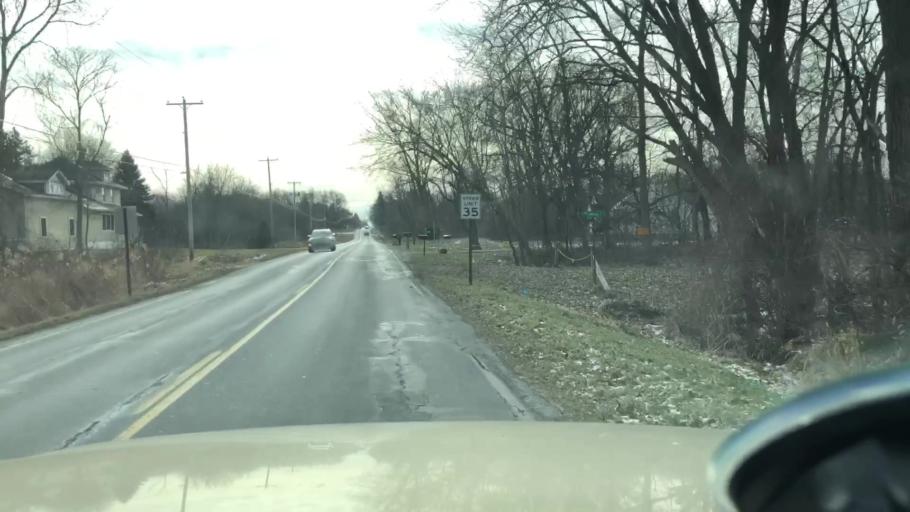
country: US
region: Michigan
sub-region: Jackson County
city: Jackson
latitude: 42.2655
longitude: -84.3650
